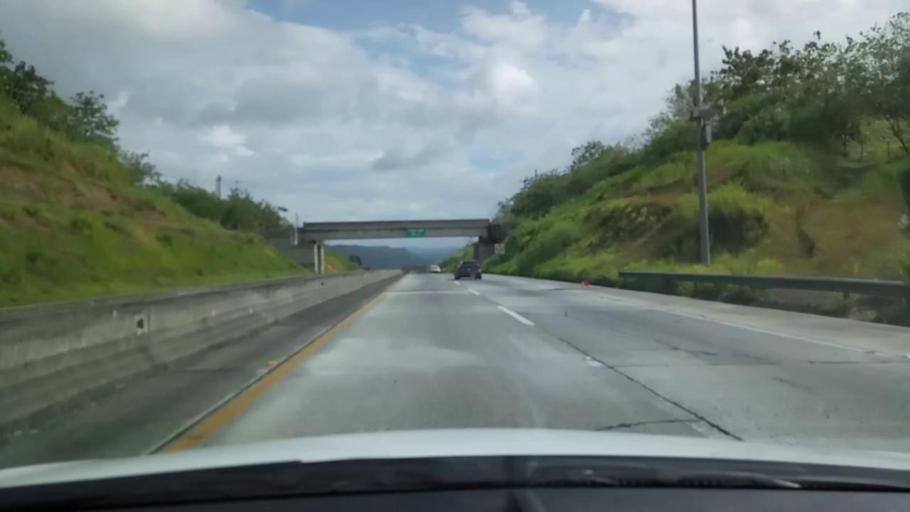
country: PA
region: Colon
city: El Giral
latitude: 9.2439
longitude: -79.6838
